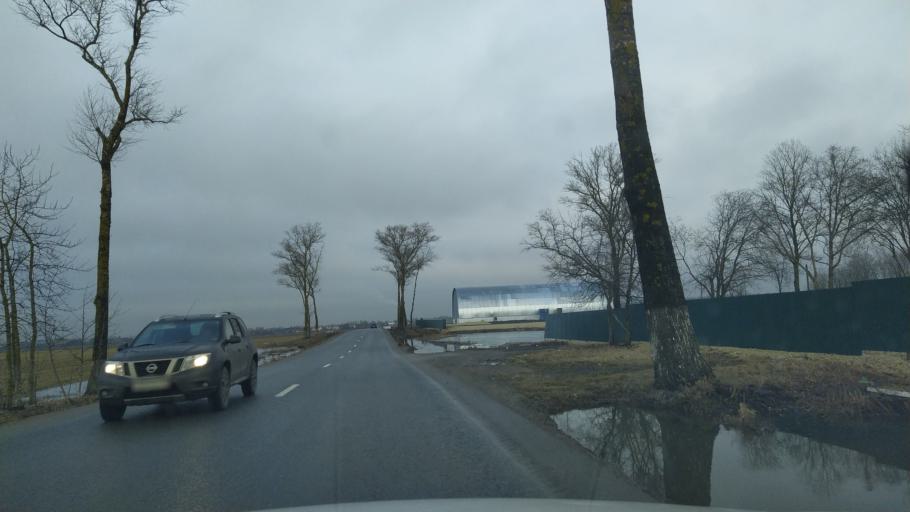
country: RU
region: St.-Petersburg
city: Aleksandrovskaya
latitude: 59.7134
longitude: 30.3329
